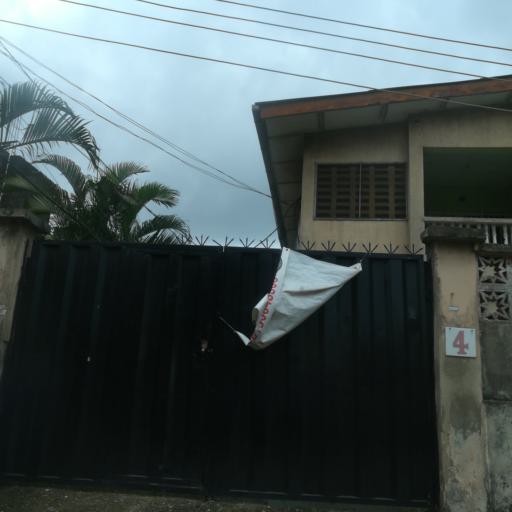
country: NG
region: Lagos
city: Agege
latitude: 6.6026
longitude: 3.2983
